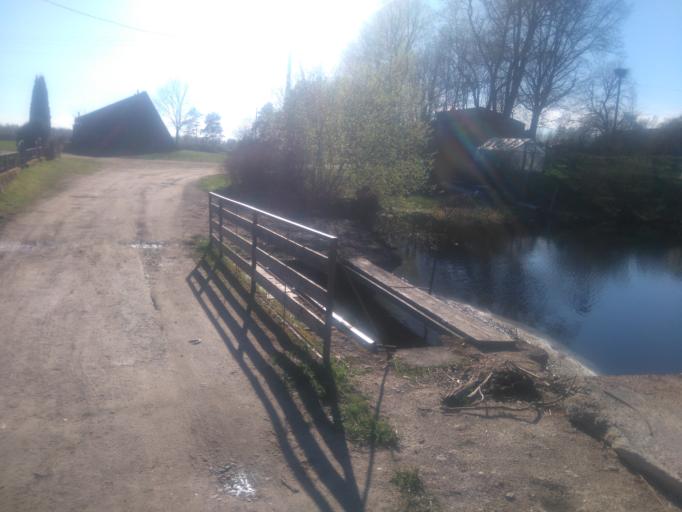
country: LV
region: Vecpiebalga
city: Vecpiebalga
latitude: 57.0168
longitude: 25.8312
